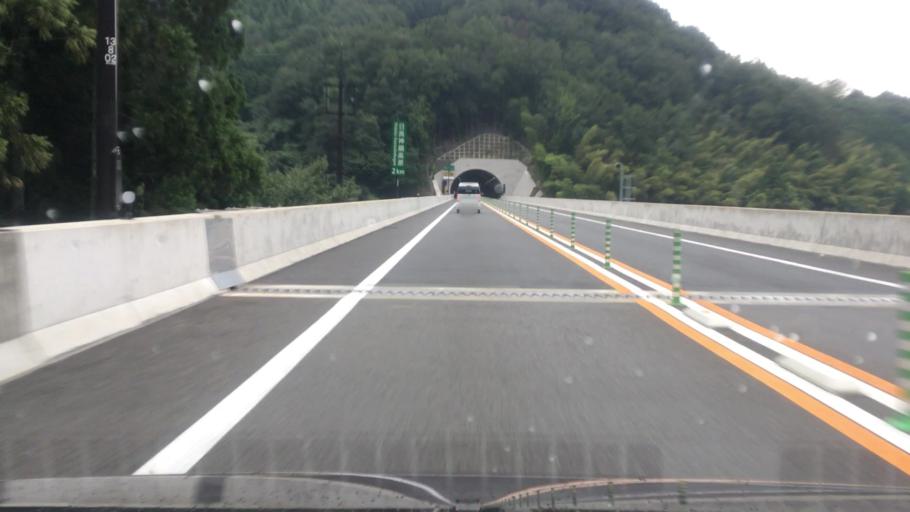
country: JP
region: Hyogo
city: Toyooka
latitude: 35.4486
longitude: 134.7659
